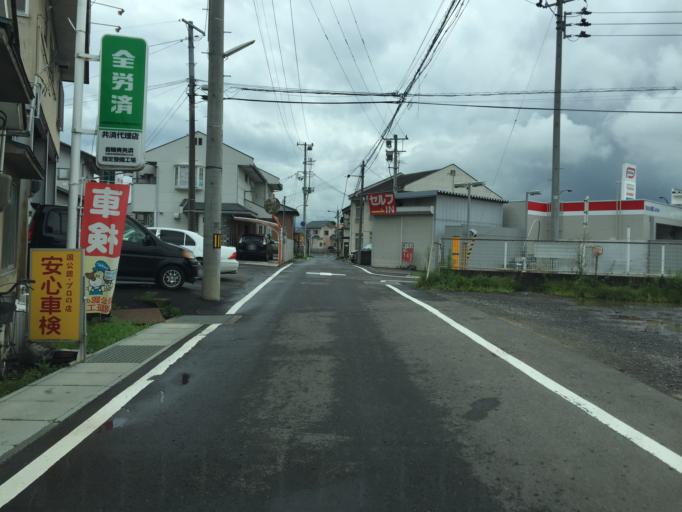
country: JP
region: Fukushima
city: Fukushima-shi
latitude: 37.7442
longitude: 140.4719
